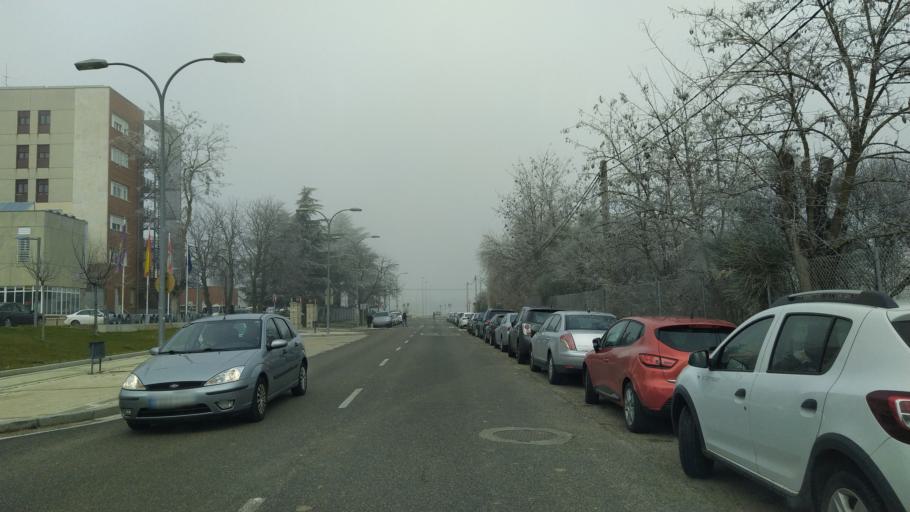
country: ES
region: Castille and Leon
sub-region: Provincia de Palencia
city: Palencia
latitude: 42.0003
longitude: -4.5384
